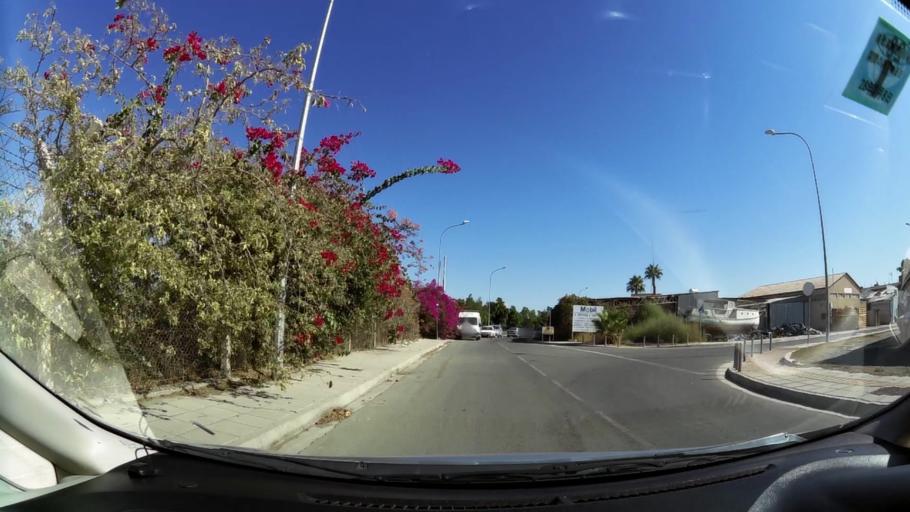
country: CY
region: Larnaka
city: Livadia
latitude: 34.9386
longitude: 33.6393
